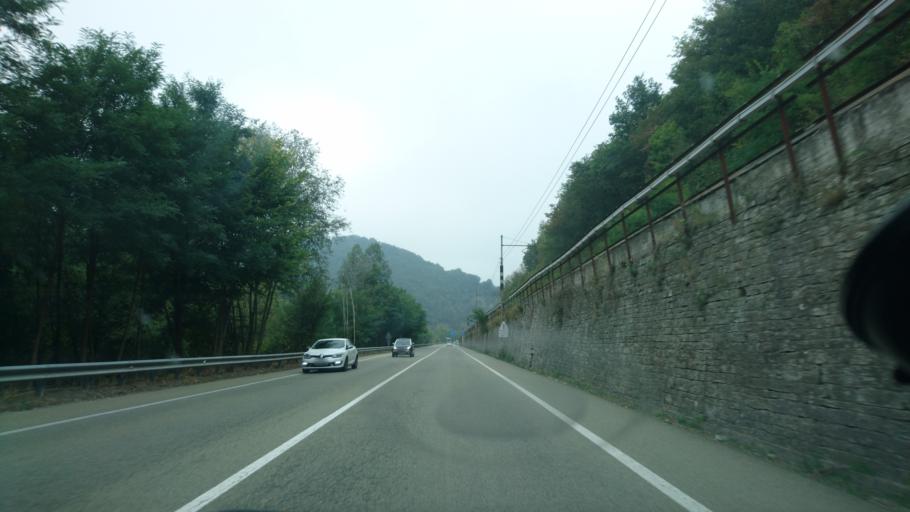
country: IT
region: Piedmont
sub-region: Provincia di Alessandria
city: Ponti
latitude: 44.6196
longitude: 8.3512
